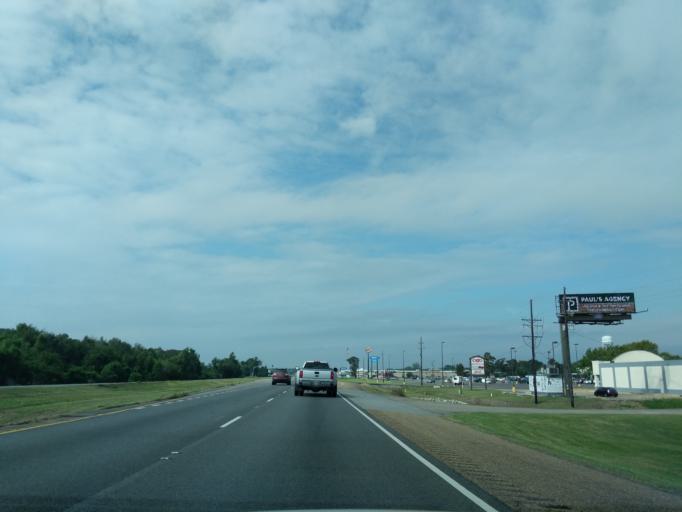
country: US
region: Louisiana
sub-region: Saint Mary Parish
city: Bayou Vista
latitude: 29.6824
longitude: -91.2638
